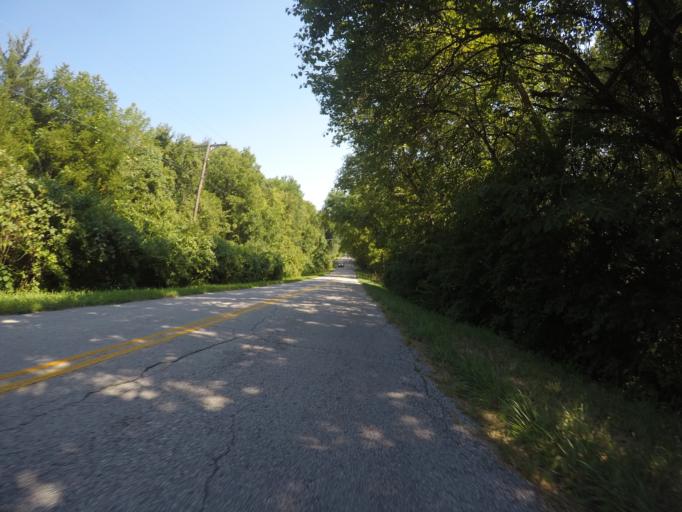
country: US
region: Kansas
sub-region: Wyandotte County
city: Edwardsville
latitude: 39.1668
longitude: -94.7929
